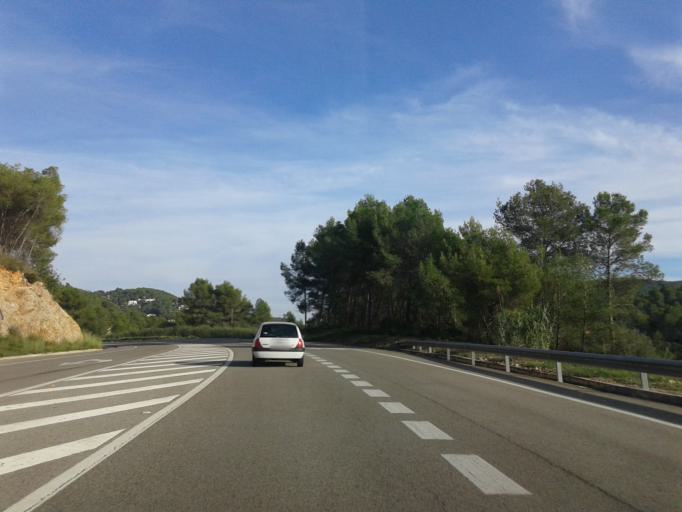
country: ES
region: Catalonia
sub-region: Provincia de Barcelona
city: Sant Pere de Ribes
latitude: 41.2864
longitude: 1.7433
